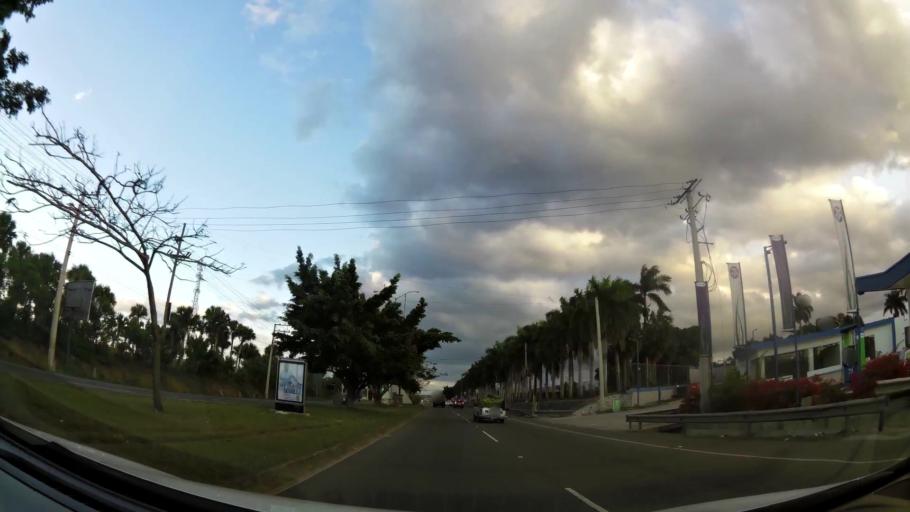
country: DO
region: Santiago
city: Licey al Medio
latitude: 19.4030
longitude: -70.6343
